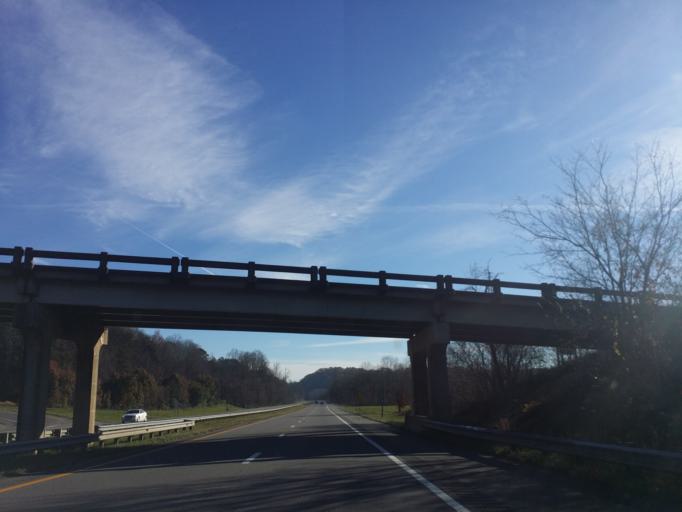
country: US
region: North Carolina
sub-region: McDowell County
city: West Marion
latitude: 35.6387
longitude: -82.1447
